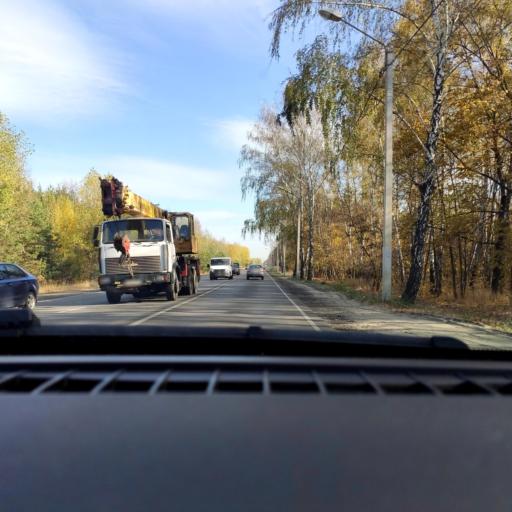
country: RU
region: Voronezj
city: Somovo
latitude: 51.6861
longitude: 39.2880
